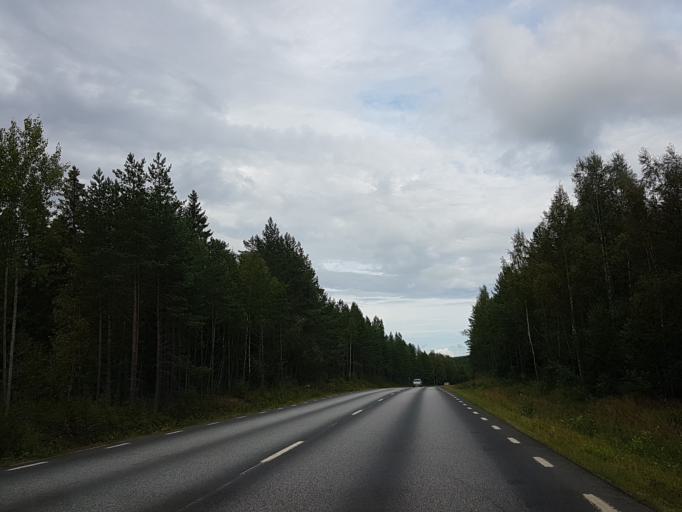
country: SE
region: Vaesterbotten
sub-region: Umea Kommun
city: Taftea
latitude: 63.8125
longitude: 20.3925
